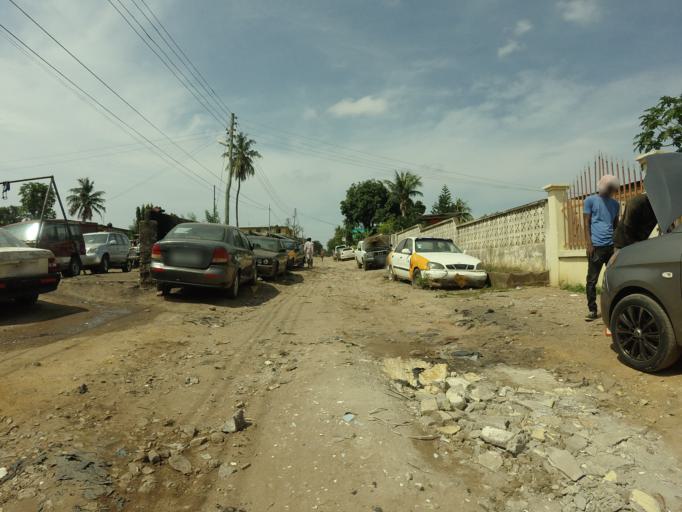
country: GH
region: Greater Accra
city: Dome
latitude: 5.6294
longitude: -0.2333
